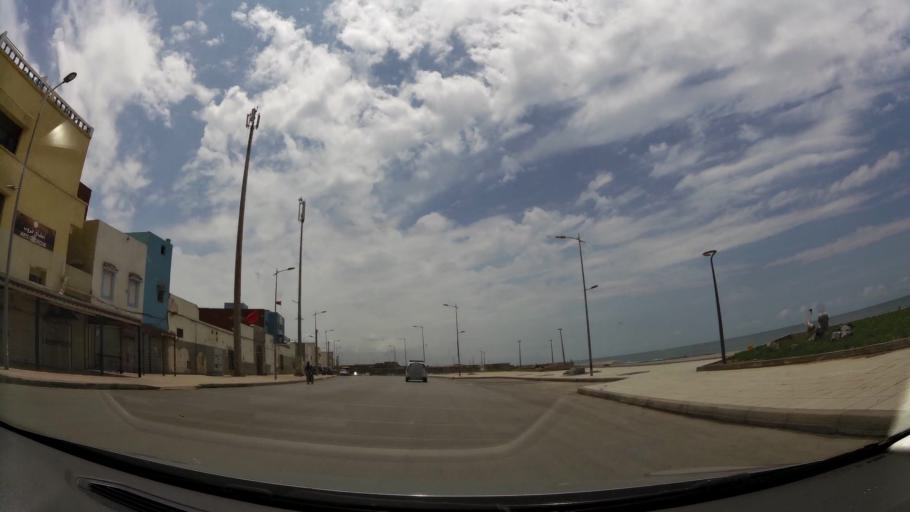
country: MA
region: Rabat-Sale-Zemmour-Zaer
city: Sale
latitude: 34.0492
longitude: -6.8271
